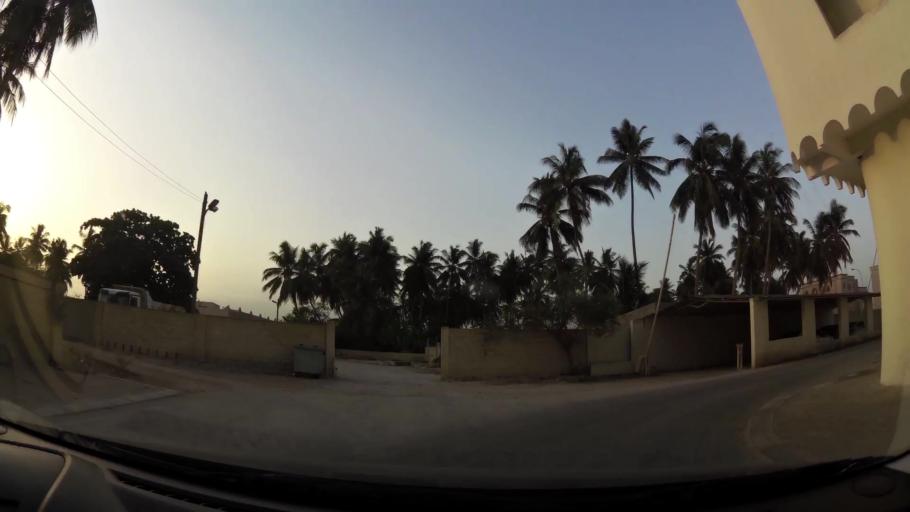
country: OM
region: Zufar
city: Salalah
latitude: 17.0178
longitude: 54.1197
